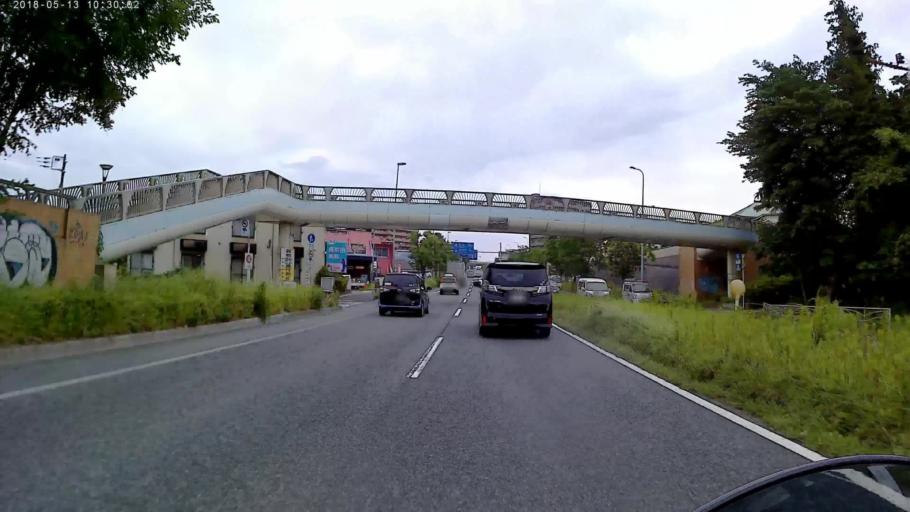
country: JP
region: Kanagawa
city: Minami-rinkan
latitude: 35.5041
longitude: 139.4708
